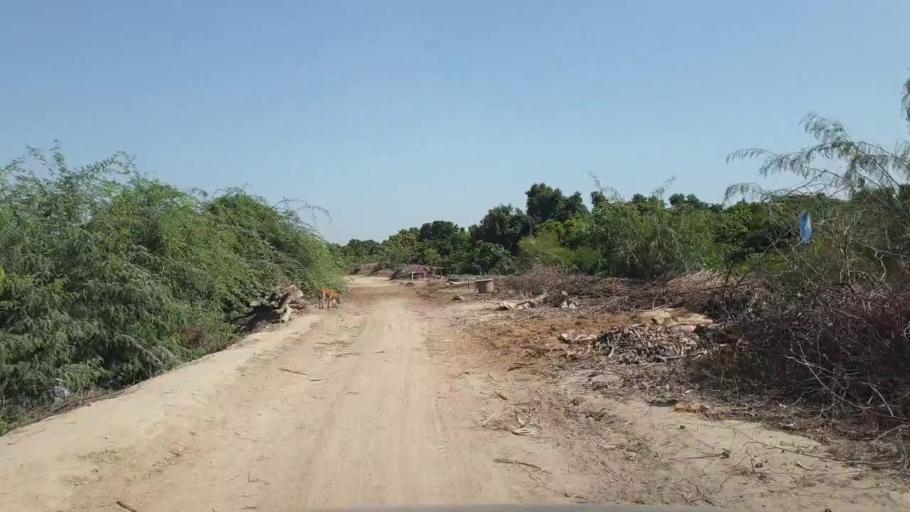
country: PK
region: Sindh
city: Matiari
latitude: 25.6260
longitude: 68.4807
